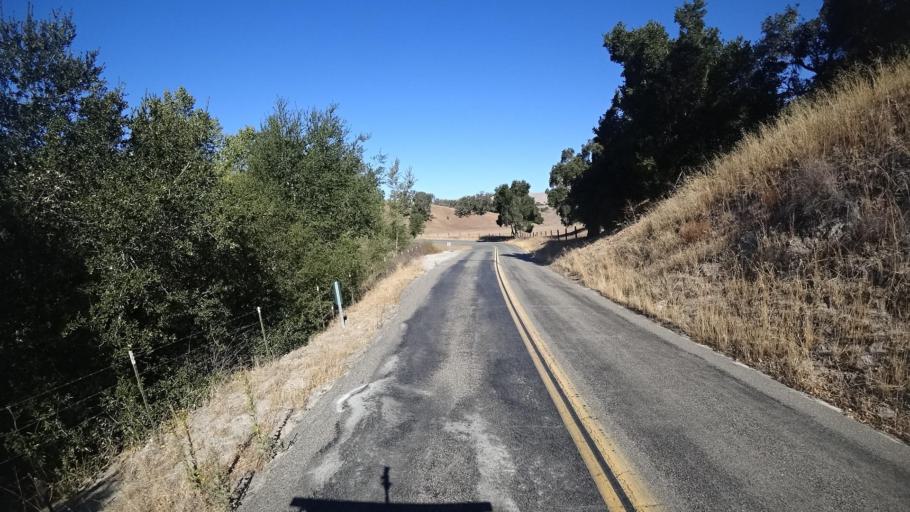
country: US
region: California
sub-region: Monterey County
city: Carmel Valley Village
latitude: 36.4401
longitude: -121.6403
